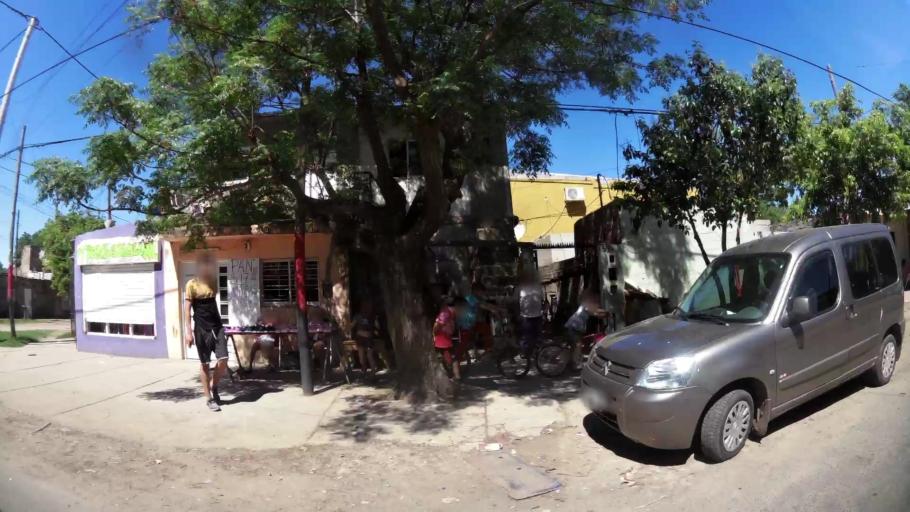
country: AR
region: Santa Fe
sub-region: Departamento de Rosario
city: Rosario
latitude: -32.9331
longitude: -60.6937
